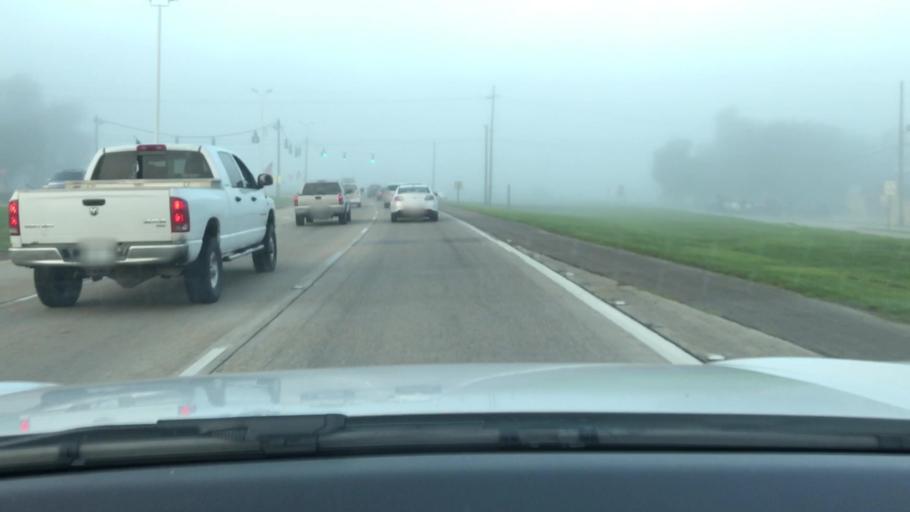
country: US
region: Louisiana
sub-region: West Baton Rouge Parish
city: Addis
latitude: 30.3650
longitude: -91.2607
